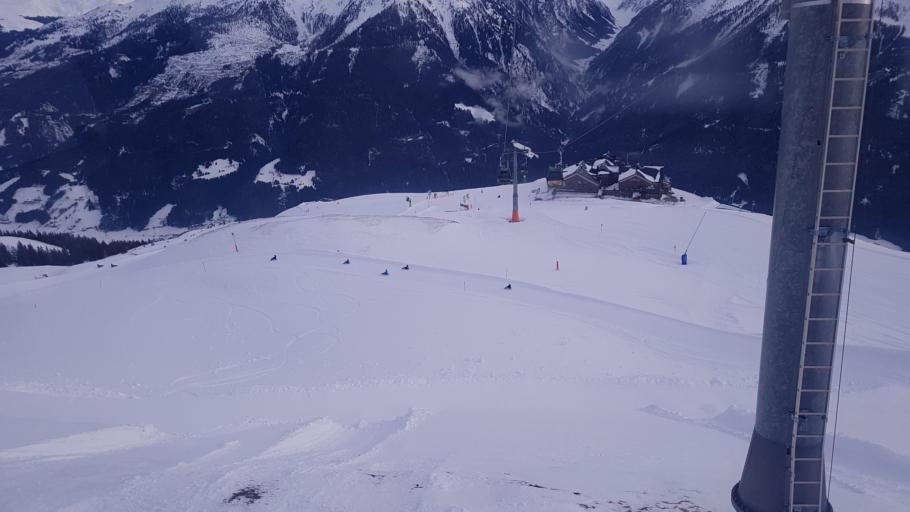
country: AT
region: Salzburg
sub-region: Politischer Bezirk Zell am See
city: Neukirchen am Grossvenediger
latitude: 47.2815
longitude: 12.2957
